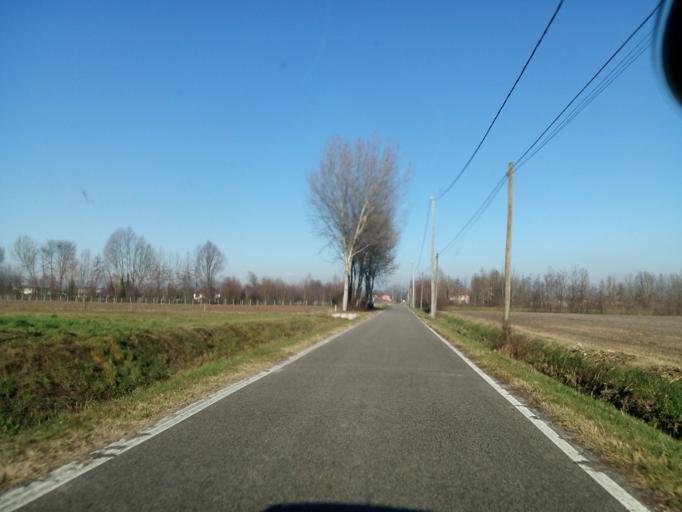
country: IT
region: Veneto
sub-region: Provincia di Venezia
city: Veternigo
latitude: 45.5243
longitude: 12.0747
